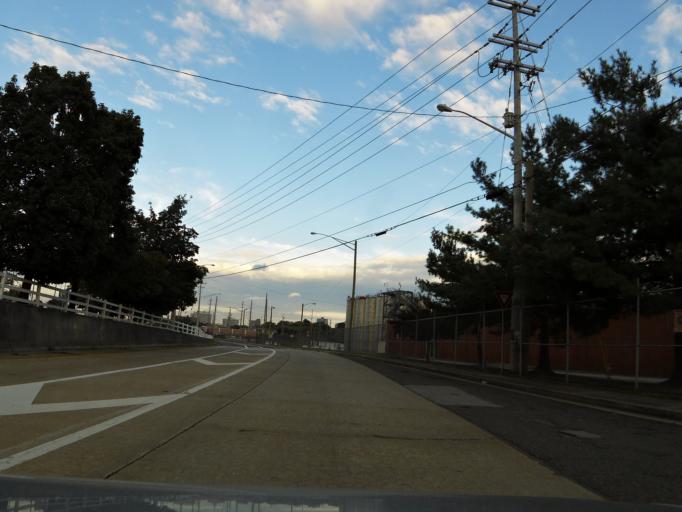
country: US
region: Tennessee
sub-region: Knox County
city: Knoxville
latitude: 35.9621
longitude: -83.9397
